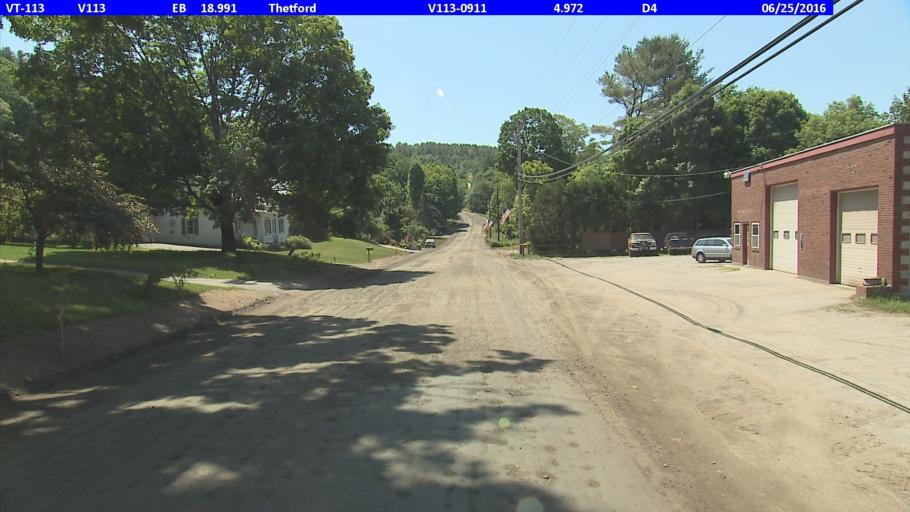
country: US
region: New Hampshire
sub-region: Grafton County
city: Lyme
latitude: 43.8303
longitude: -72.2468
